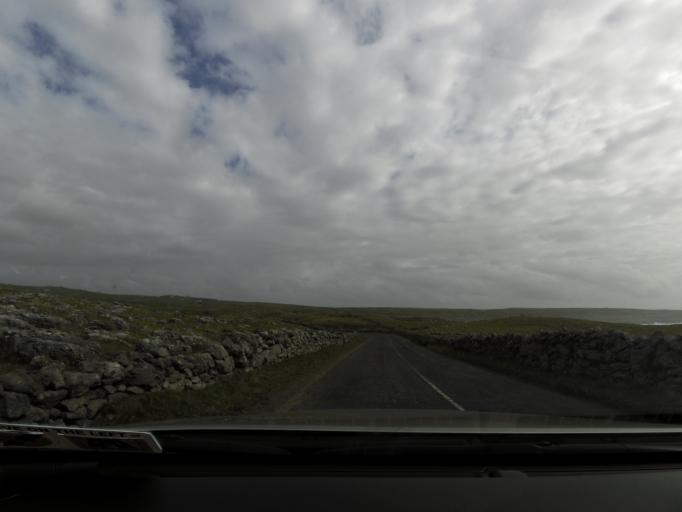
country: IE
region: Connaught
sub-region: County Galway
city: Bearna
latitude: 53.0600
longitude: -9.3620
